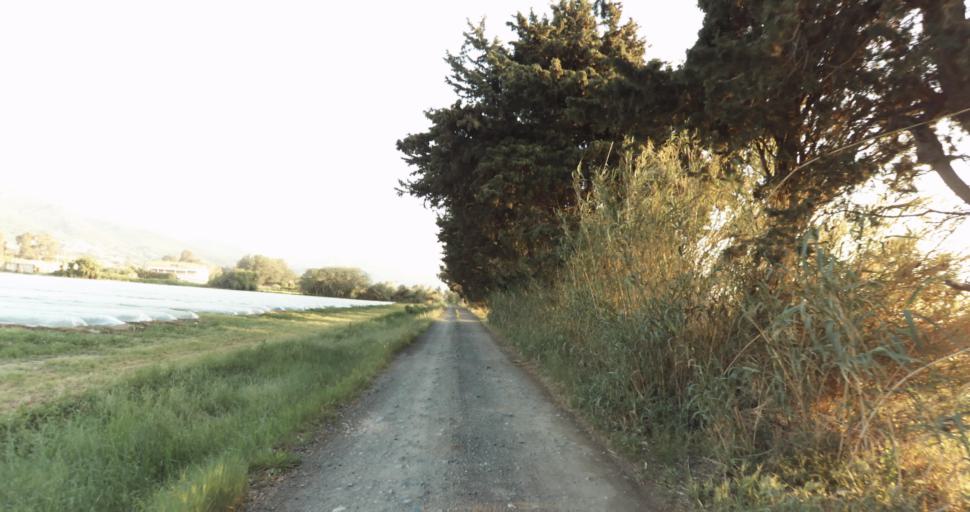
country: FR
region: Corsica
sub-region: Departement de la Haute-Corse
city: Biguglia
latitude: 42.6112
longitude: 9.4471
